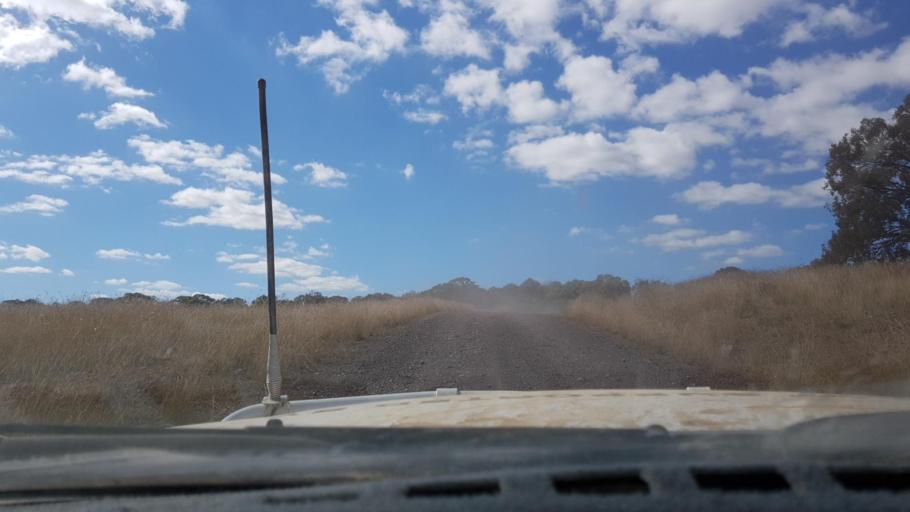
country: AU
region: New South Wales
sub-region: Tamworth Municipality
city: Manilla
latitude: -30.4269
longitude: 150.8126
